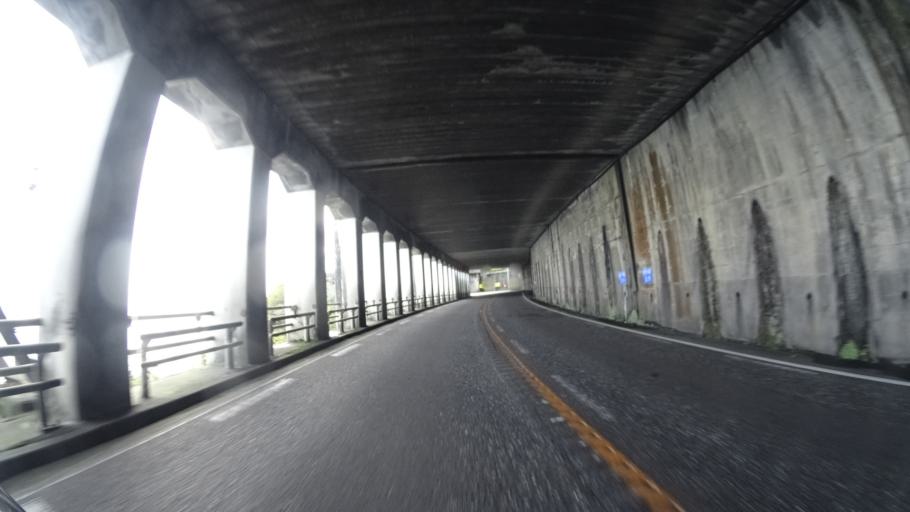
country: JP
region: Niigata
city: Itoigawa
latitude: 36.9899
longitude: 137.6814
